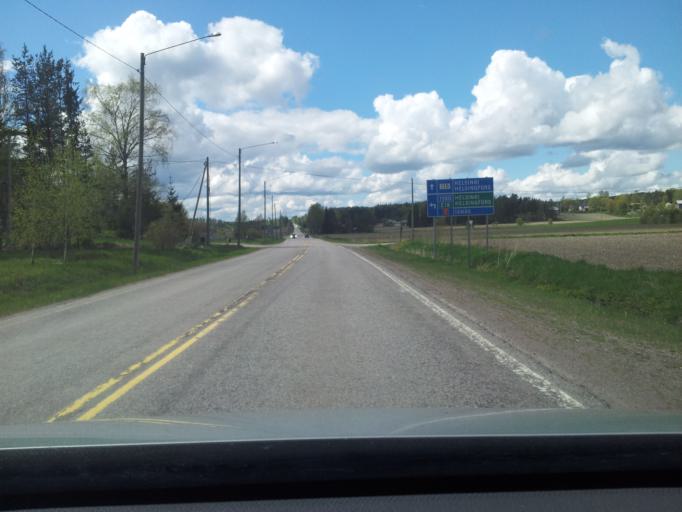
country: FI
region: Uusimaa
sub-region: Loviisa
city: Perna
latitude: 60.4937
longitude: 25.8971
